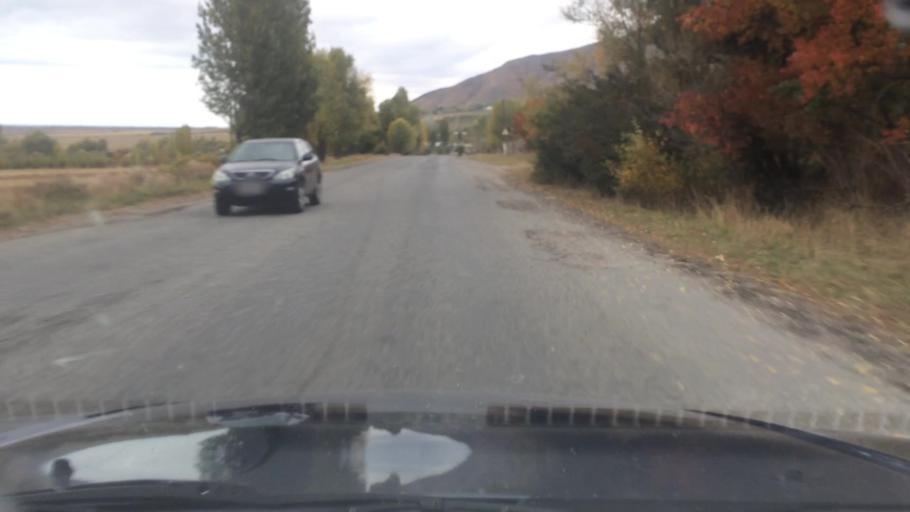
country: KG
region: Ysyk-Koel
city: Tyup
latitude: 42.7475
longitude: 78.0973
